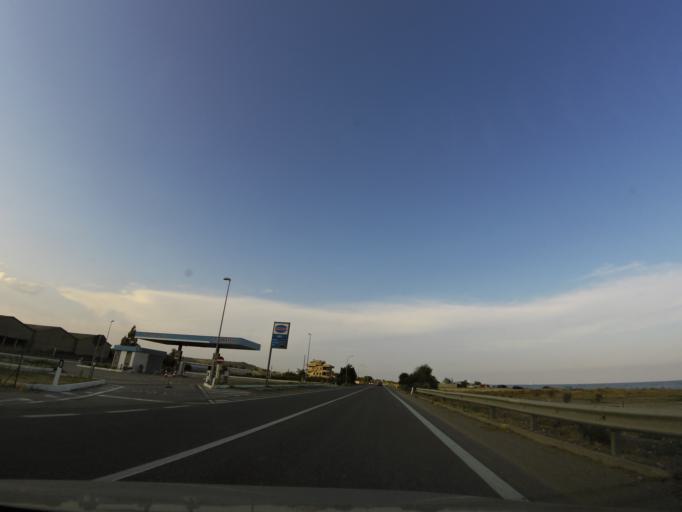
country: IT
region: Calabria
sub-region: Provincia di Reggio Calabria
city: Monasterace Marina
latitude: 38.4190
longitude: 16.5623
